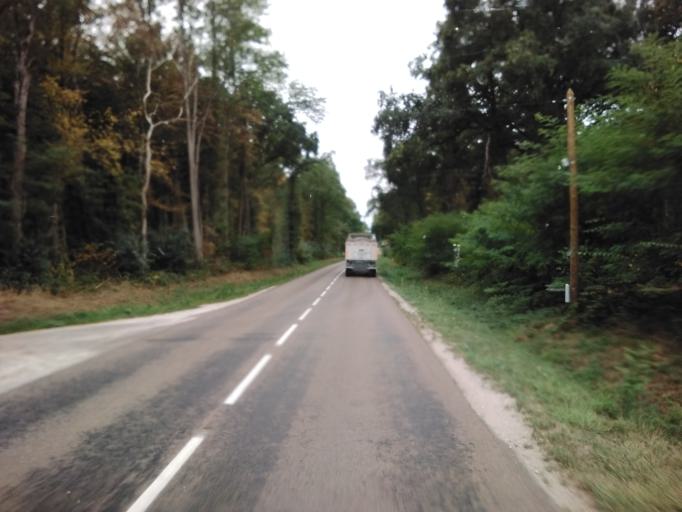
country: FR
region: Champagne-Ardenne
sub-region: Departement de l'Aube
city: Vendeuvre-sur-Barse
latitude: 48.2526
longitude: 4.4898
